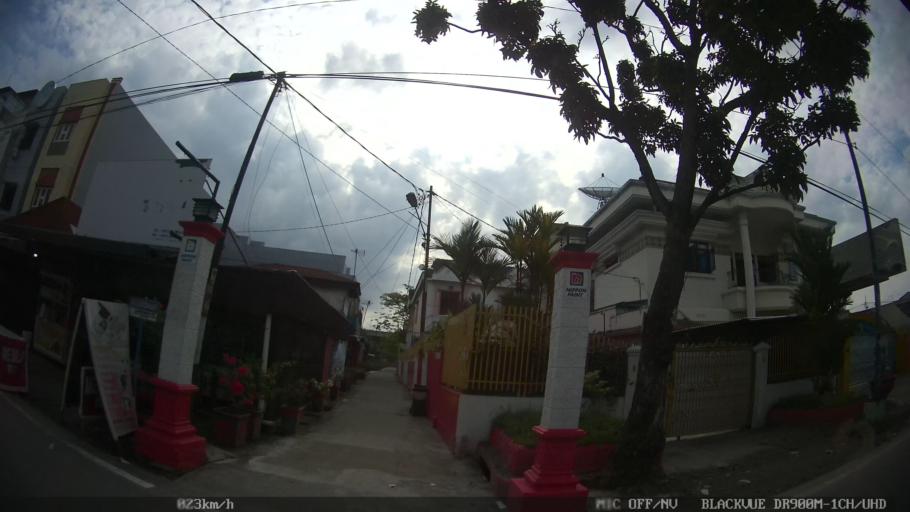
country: ID
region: North Sumatra
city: Medan
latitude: 3.6027
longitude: 98.6768
